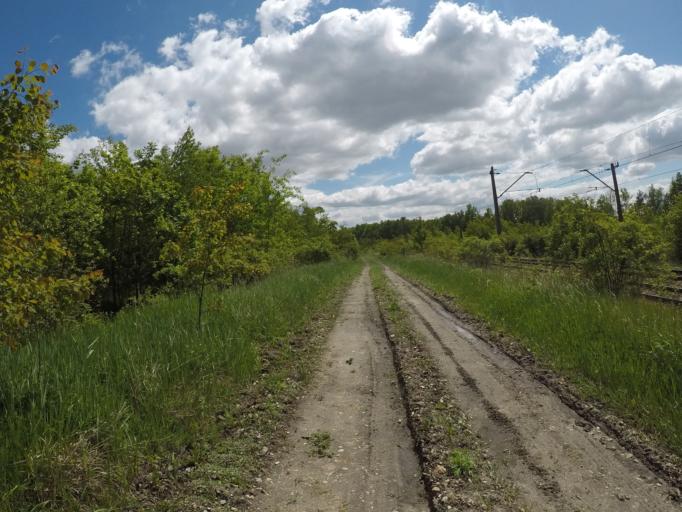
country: PL
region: Swietokrzyskie
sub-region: Powiat kielecki
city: Kostomloty Pierwsze
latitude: 50.9277
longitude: 20.6042
